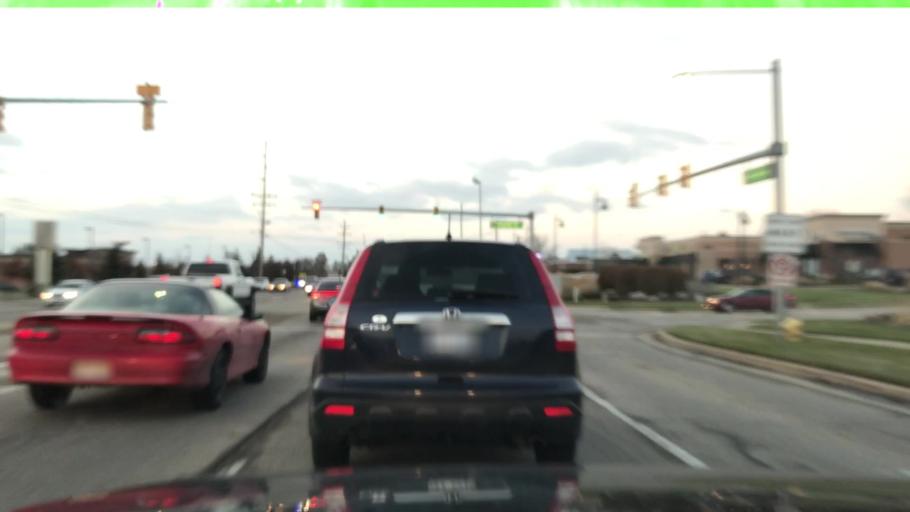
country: US
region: Michigan
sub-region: Kent County
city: Byron Center
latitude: 42.8596
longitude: -85.7230
